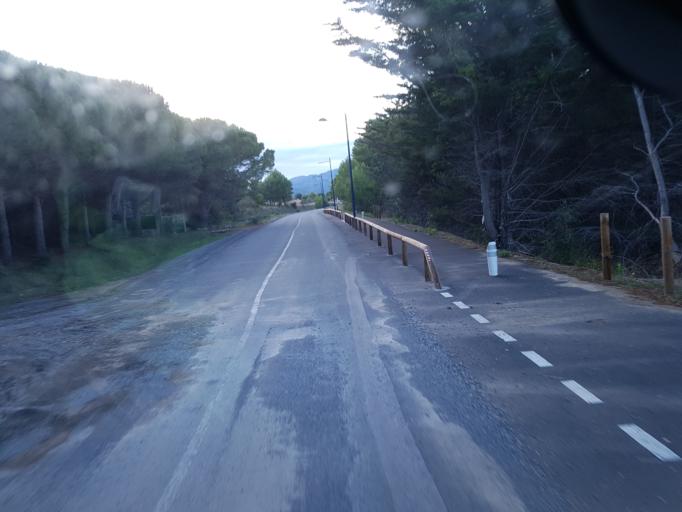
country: FR
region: Languedoc-Roussillon
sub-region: Departement de l'Aude
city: Leucate
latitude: 42.9337
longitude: 3.0193
